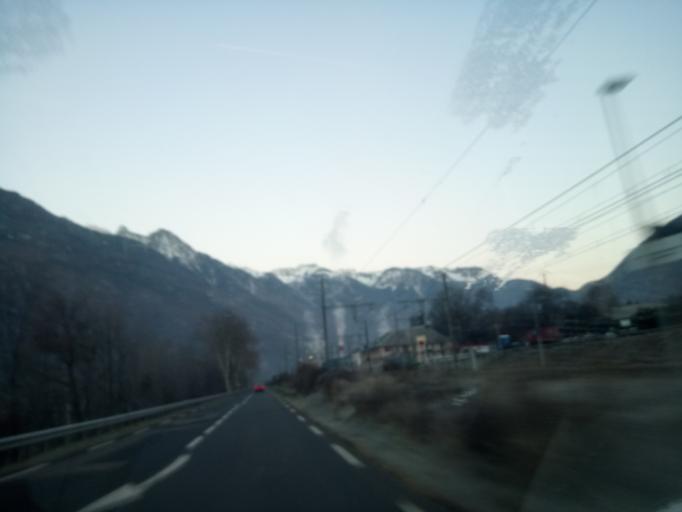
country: FR
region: Rhone-Alpes
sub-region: Departement de la Savoie
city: La Chambre
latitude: 45.3535
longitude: 6.3016
